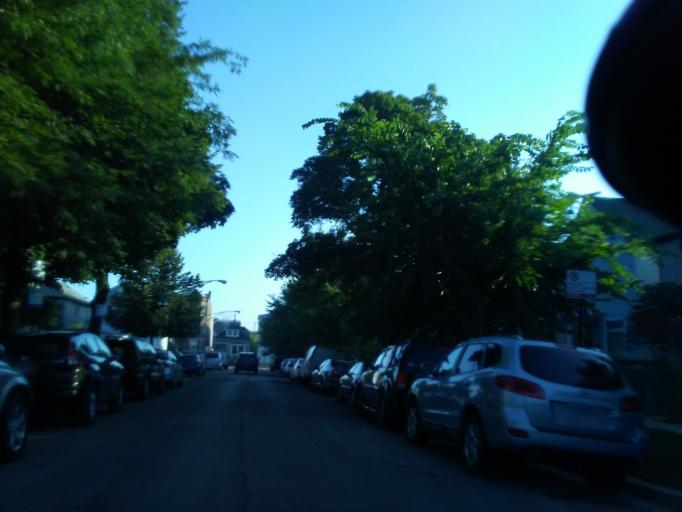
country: US
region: Illinois
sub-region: Cook County
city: Lincolnwood
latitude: 41.9311
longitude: -87.7147
